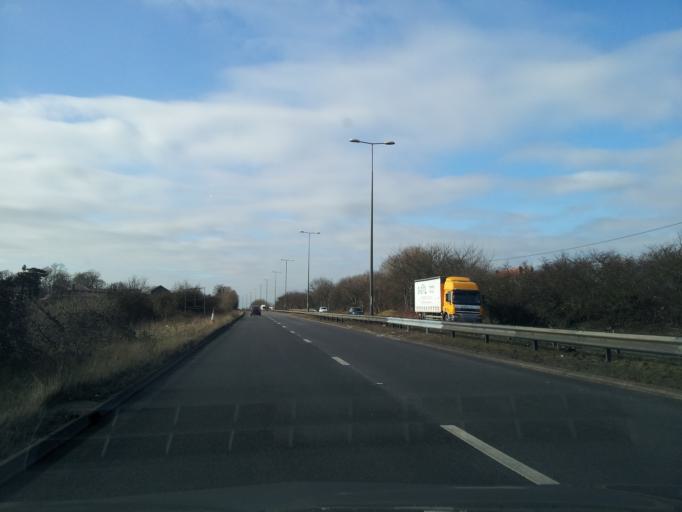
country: GB
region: England
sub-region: Derbyshire
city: Borrowash
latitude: 52.9114
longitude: -1.3402
